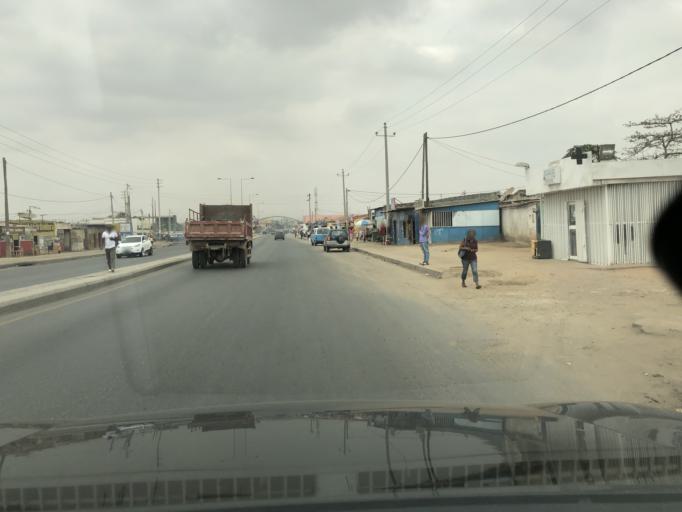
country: AO
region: Luanda
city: Luanda
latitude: -8.8333
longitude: 13.2832
